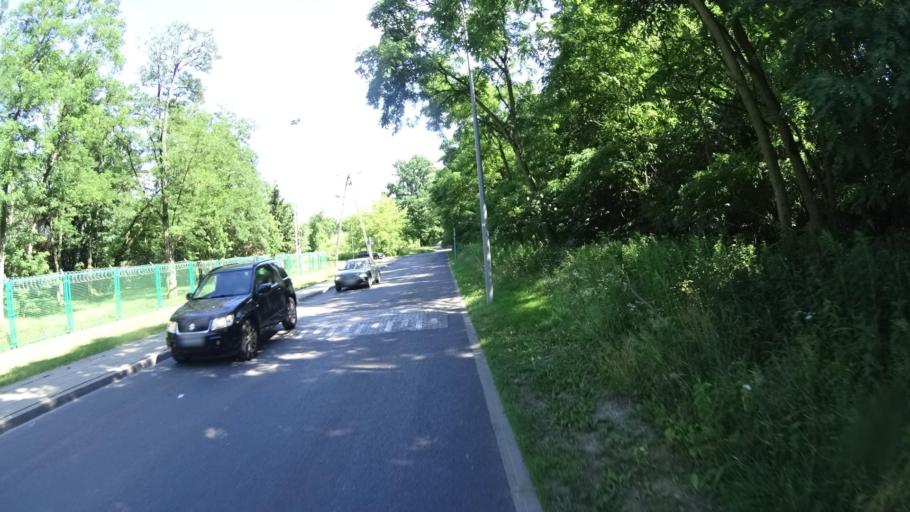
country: PL
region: Masovian Voivodeship
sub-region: Warszawa
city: Bialoleka
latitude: 52.3501
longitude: 20.9614
